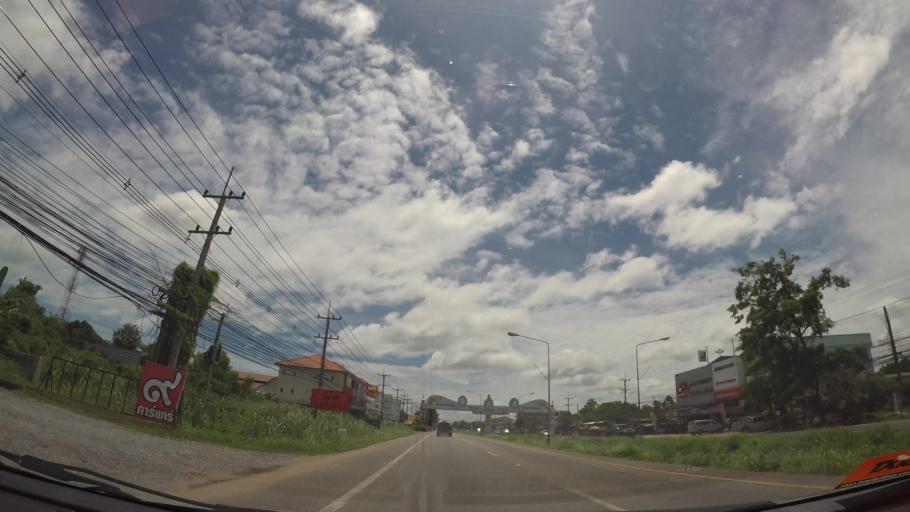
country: TH
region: Chon Buri
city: Sattahip
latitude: 12.7312
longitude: 100.8908
